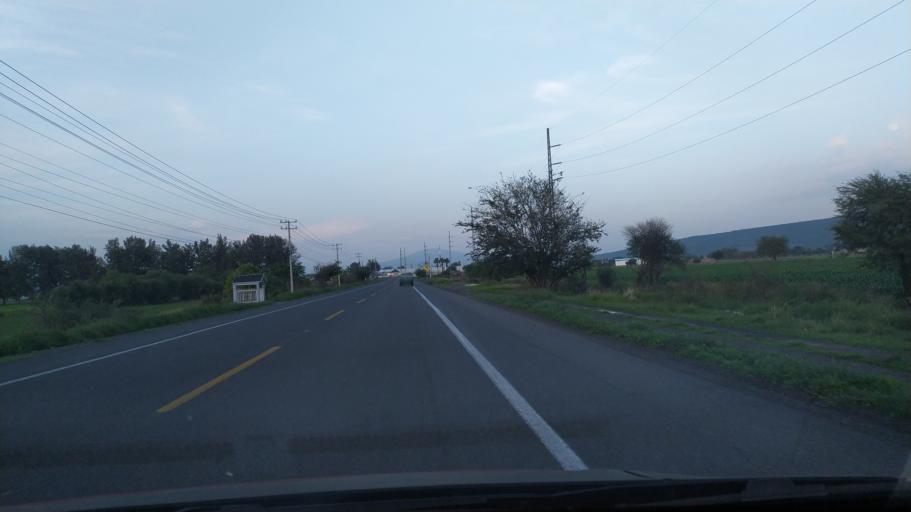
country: MX
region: Michoacan
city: Tanhuato de Guerrero
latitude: 20.2825
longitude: -102.3477
